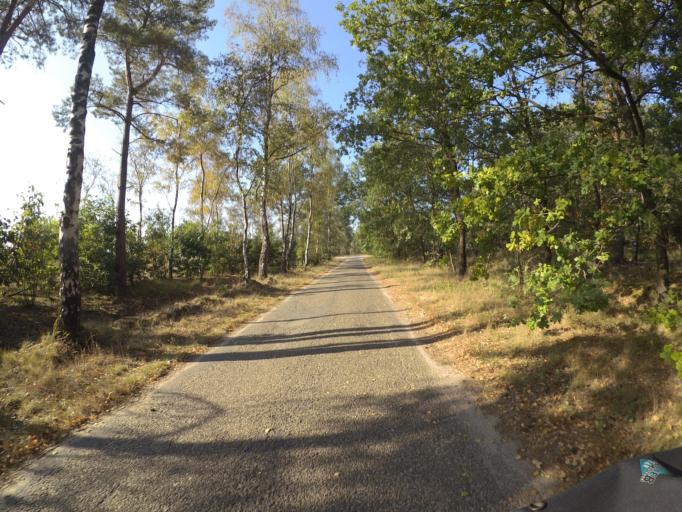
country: NL
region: North Brabant
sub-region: Gemeente Oirschot
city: Oirschot
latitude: 51.4788
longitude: 5.3262
